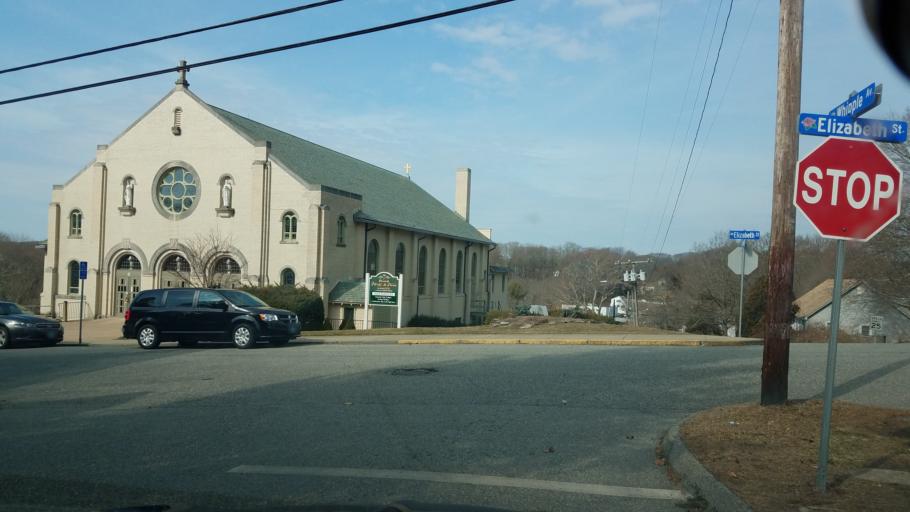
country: US
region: Connecticut
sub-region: New London County
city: Norwich
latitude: 41.5183
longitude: -72.0909
